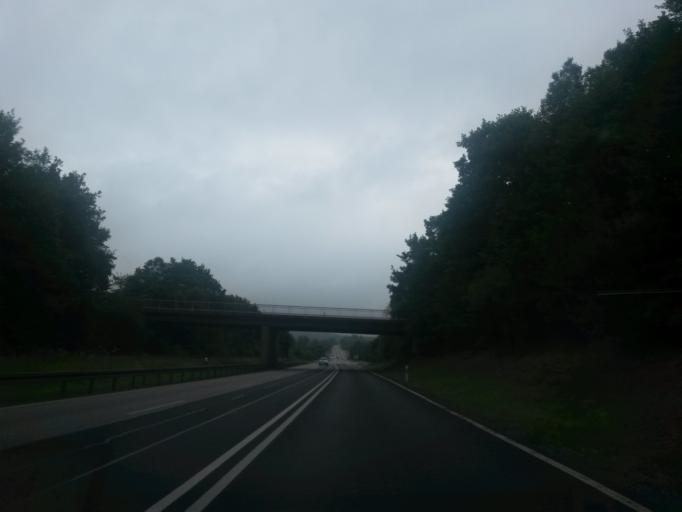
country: DE
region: Bavaria
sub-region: Upper Palatinate
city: Amberg
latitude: 49.4429
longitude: 11.8308
